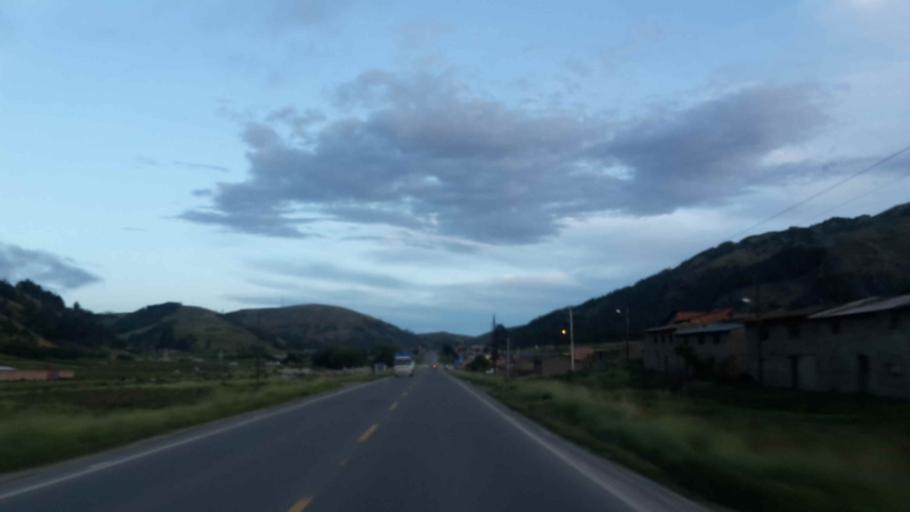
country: BO
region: Cochabamba
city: Colomi
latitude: -17.3538
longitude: -65.8506
